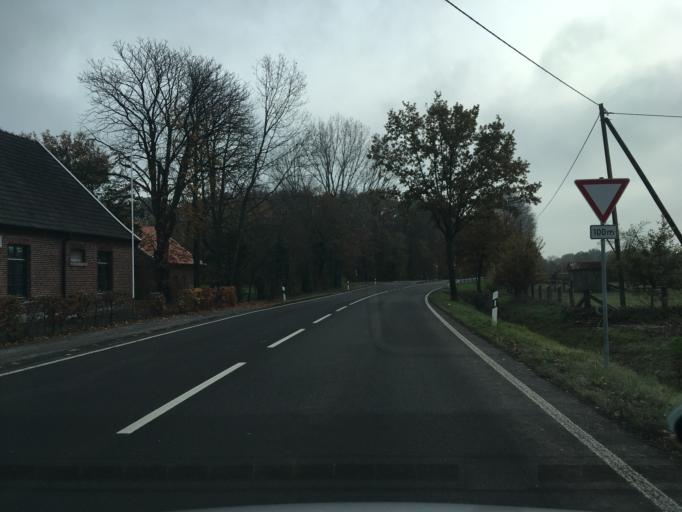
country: DE
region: North Rhine-Westphalia
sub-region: Regierungsbezirk Munster
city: Sudlohn
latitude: 51.9291
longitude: 6.8829
